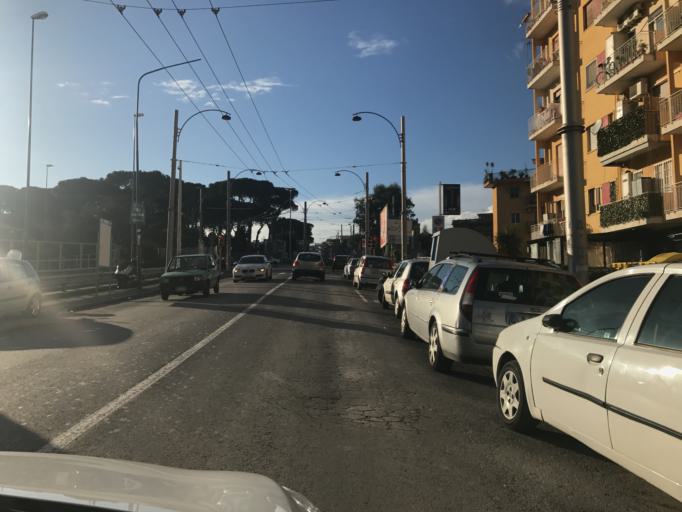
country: IT
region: Campania
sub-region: Provincia di Napoli
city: Napoli
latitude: 40.8685
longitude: 14.2292
